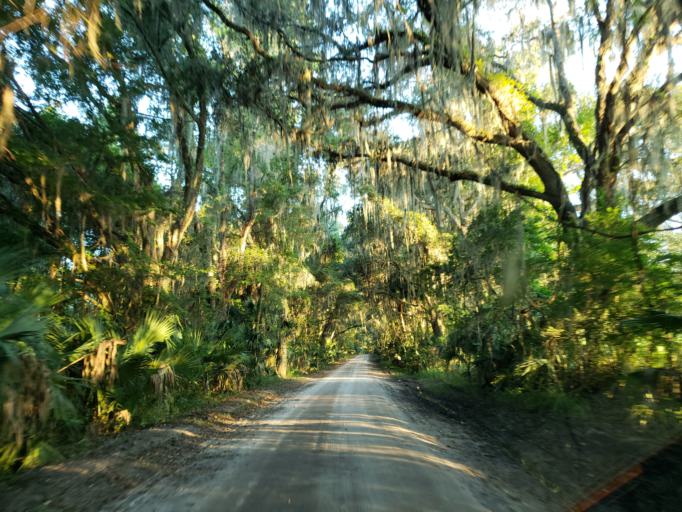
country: US
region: Florida
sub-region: Alachua County
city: Gainesville
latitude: 29.4908
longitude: -82.2795
